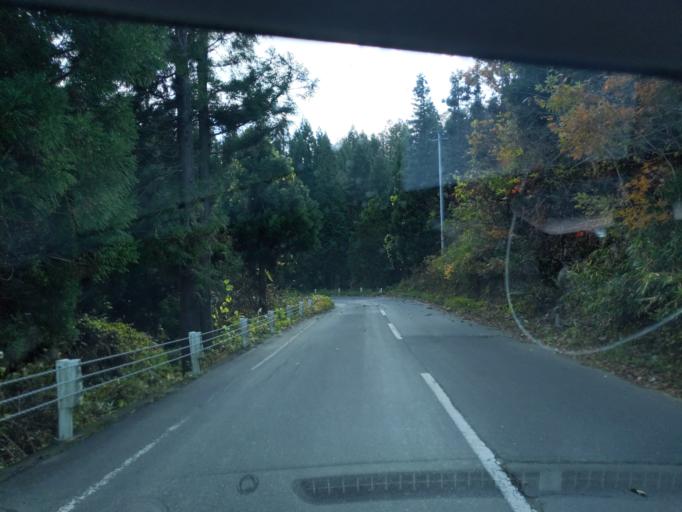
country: JP
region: Iwate
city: Mizusawa
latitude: 39.0418
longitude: 141.0951
